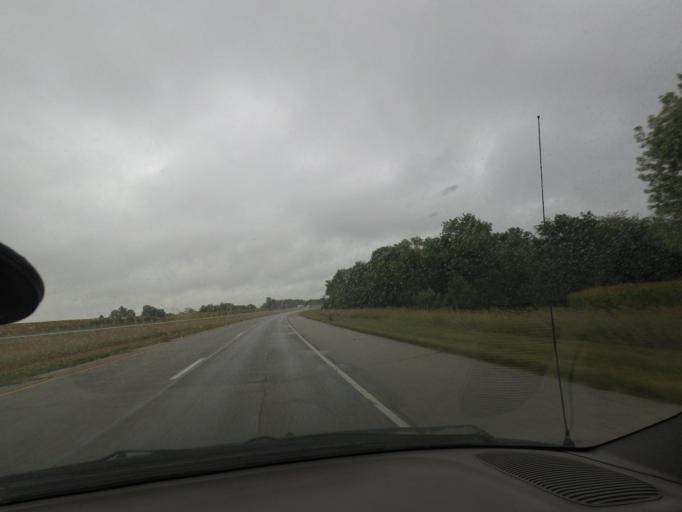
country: US
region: Illinois
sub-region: Pike County
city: Barry
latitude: 39.7392
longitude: -91.1312
